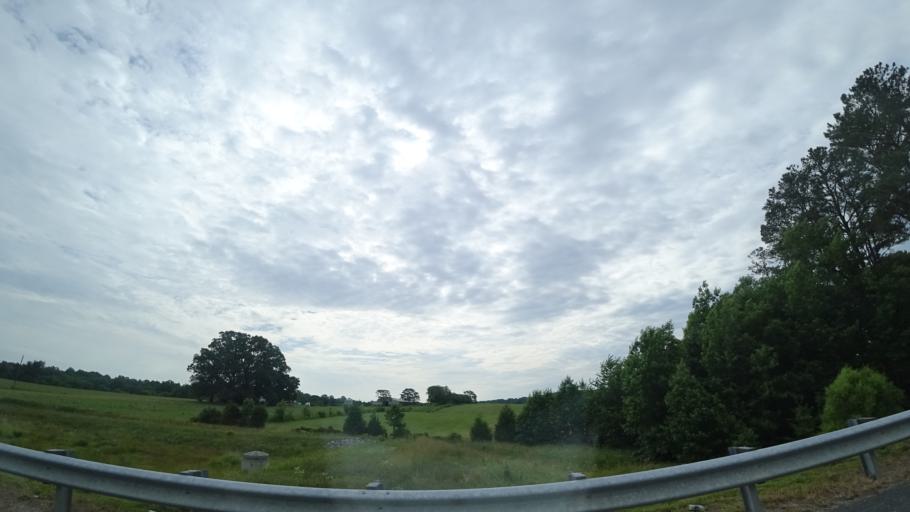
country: US
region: Virginia
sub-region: Spotsylvania County
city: Spotsylvania
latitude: 38.1877
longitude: -77.6197
